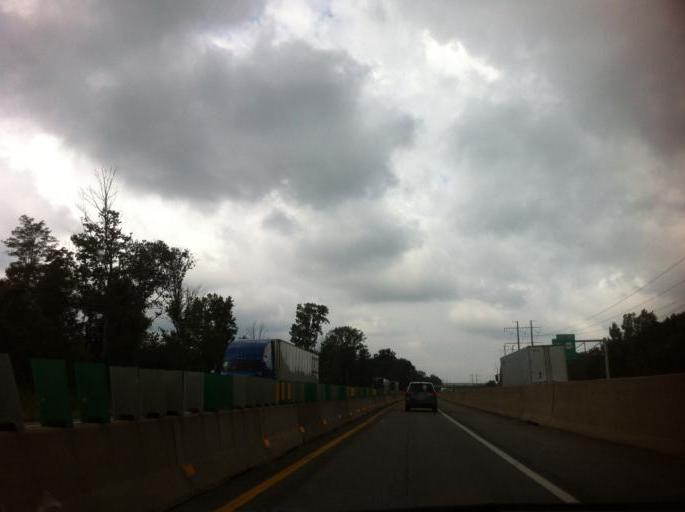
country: US
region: Ohio
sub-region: Cuyahoga County
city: Middleburg Heights
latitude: 41.3205
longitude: -81.7796
